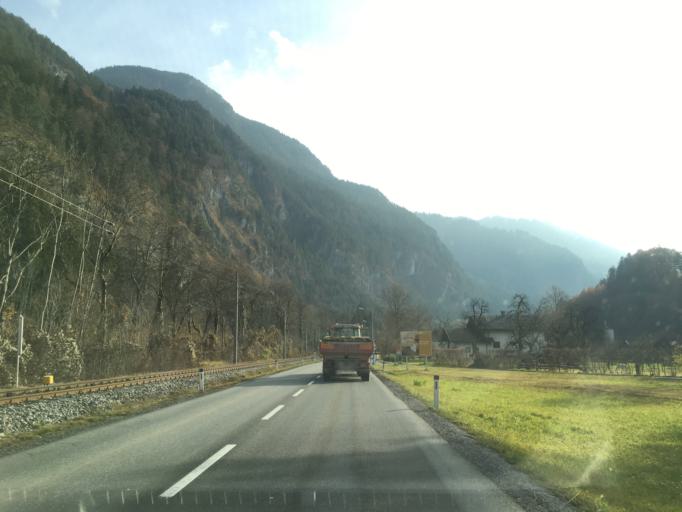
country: AT
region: Vorarlberg
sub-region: Politischer Bezirk Bludenz
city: Stallehr
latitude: 47.1317
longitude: 9.8505
